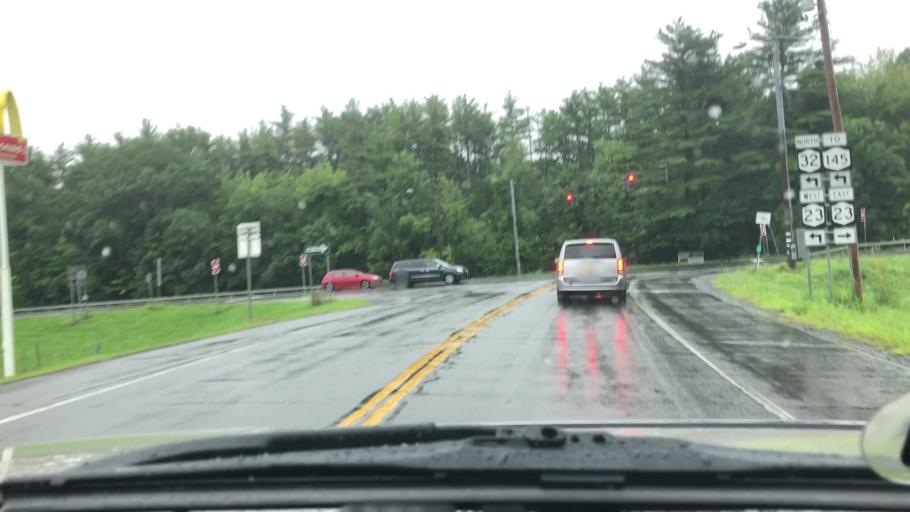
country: US
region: New York
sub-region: Greene County
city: Cairo
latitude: 42.2964
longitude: -73.9893
